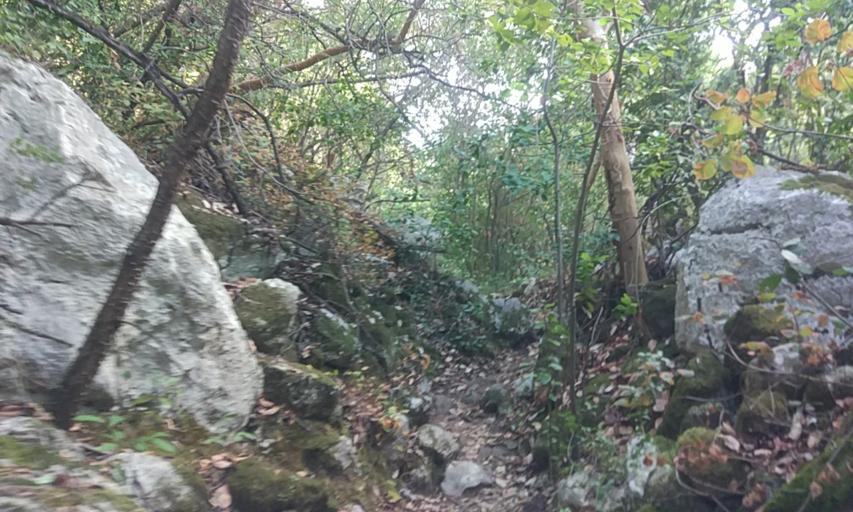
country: TR
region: Antalya
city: Tekirova
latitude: 36.3820
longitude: 30.4750
